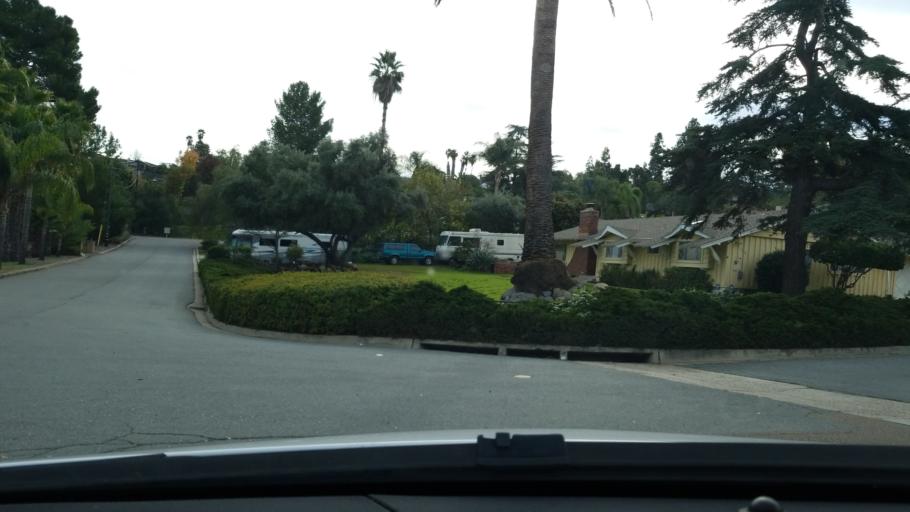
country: US
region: California
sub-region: San Diego County
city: Casa de Oro-Mount Helix
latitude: 32.7727
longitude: -116.9451
